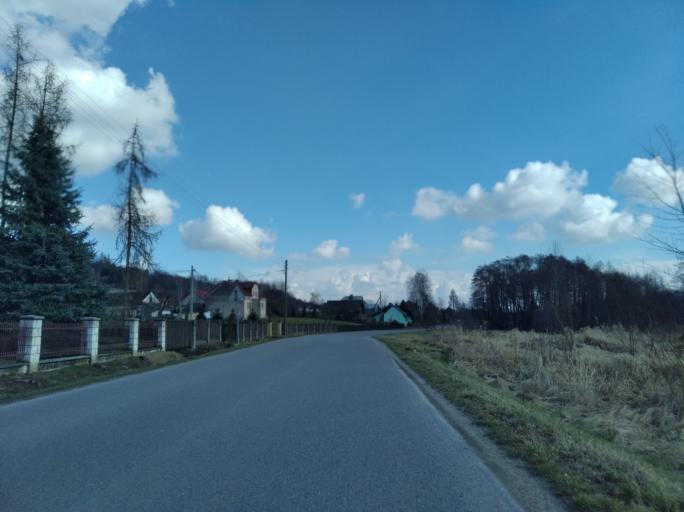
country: PL
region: Subcarpathian Voivodeship
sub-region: Powiat debicki
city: Brzostek
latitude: 49.8622
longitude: 21.4647
